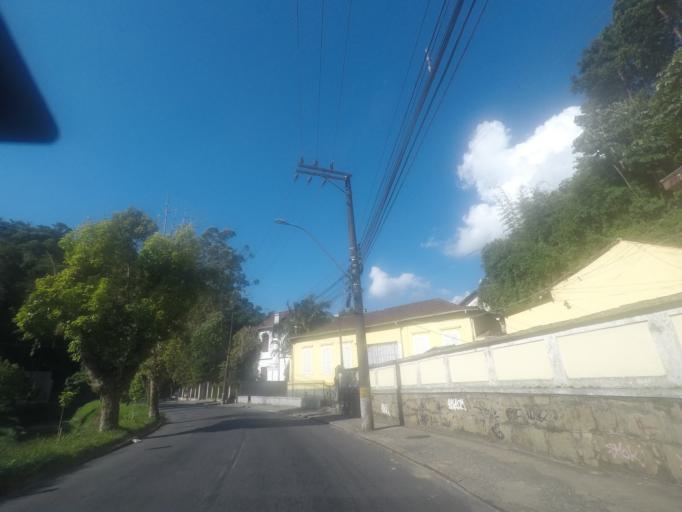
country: BR
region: Rio de Janeiro
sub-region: Petropolis
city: Petropolis
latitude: -22.5118
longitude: -43.1709
